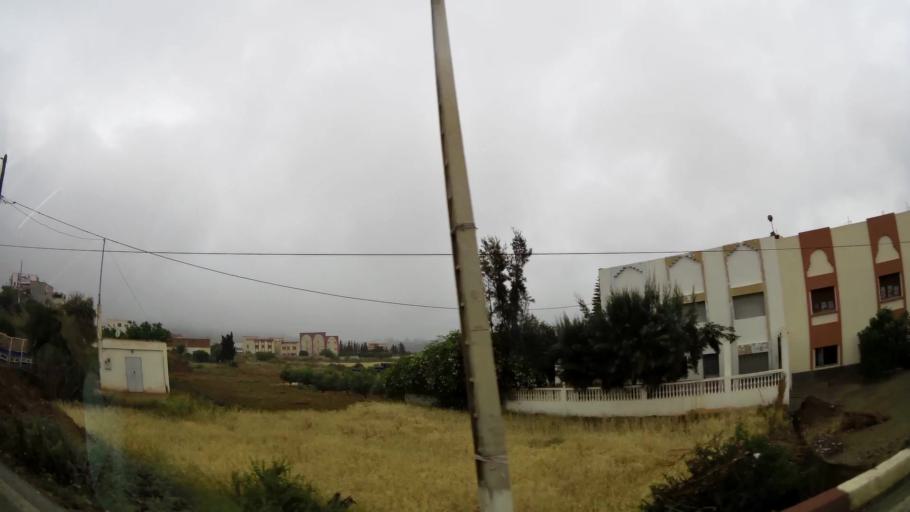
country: MA
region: Taza-Al Hoceima-Taounate
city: Imzourene
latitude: 35.1963
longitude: -3.8978
